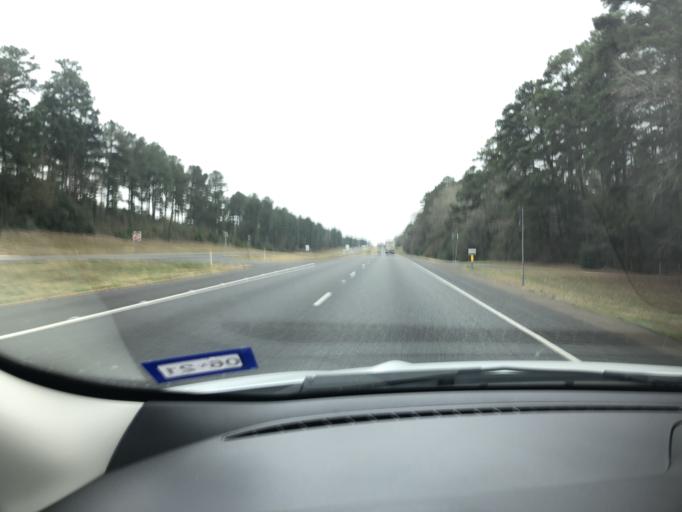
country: US
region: Texas
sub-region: Nacogdoches County
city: Nacogdoches
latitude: 31.5176
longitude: -94.6979
